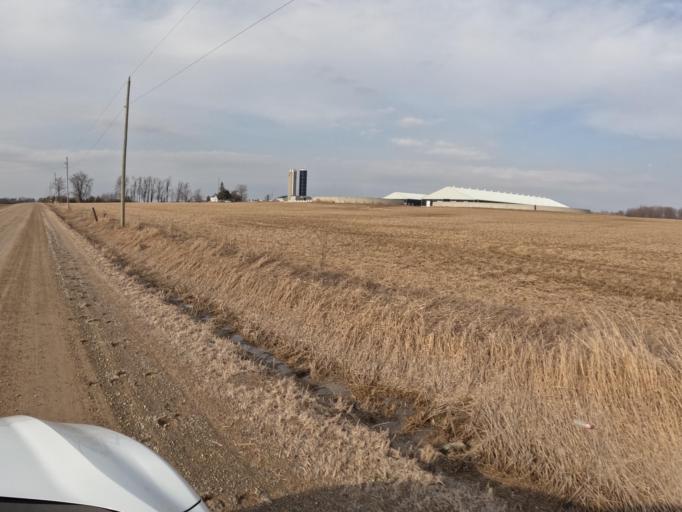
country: CA
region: Ontario
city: Orangeville
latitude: 43.9014
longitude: -80.2681
